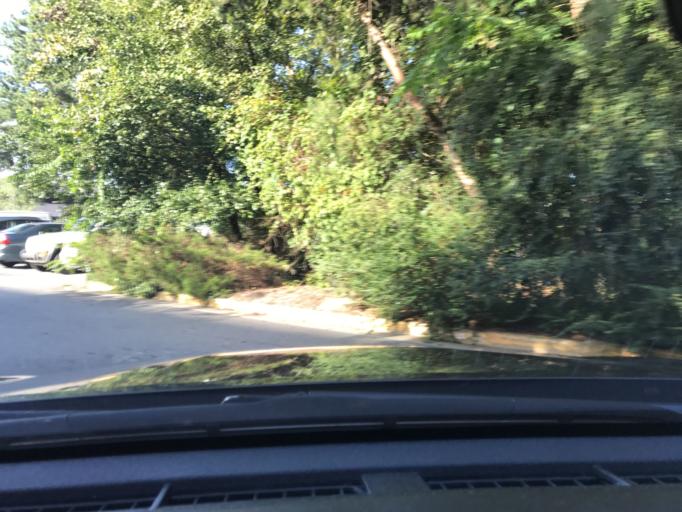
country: US
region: Georgia
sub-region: DeKalb County
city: Scottdale
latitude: 33.7914
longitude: -84.2843
